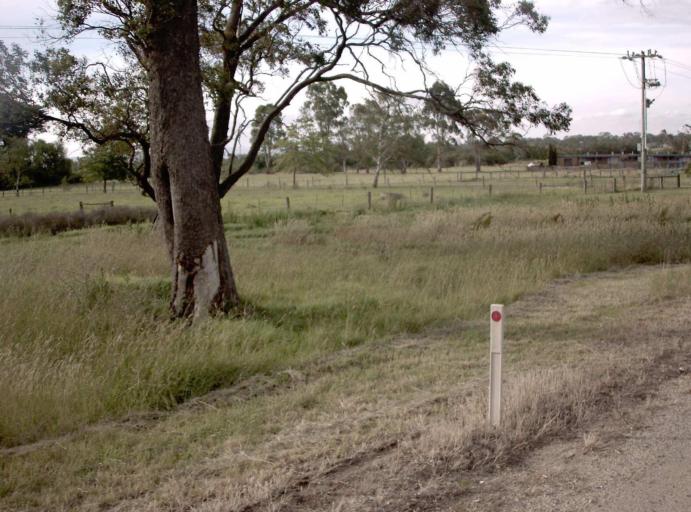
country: AU
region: Victoria
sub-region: Wellington
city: Heyfield
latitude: -37.9907
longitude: 146.7761
